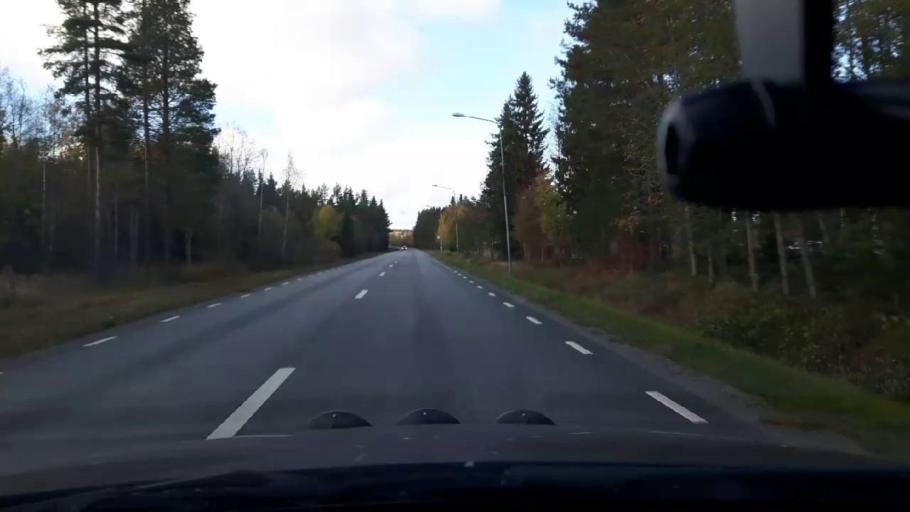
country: SE
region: Jaemtland
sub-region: Bergs Kommun
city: Hoverberg
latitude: 62.9808
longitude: 14.4521
